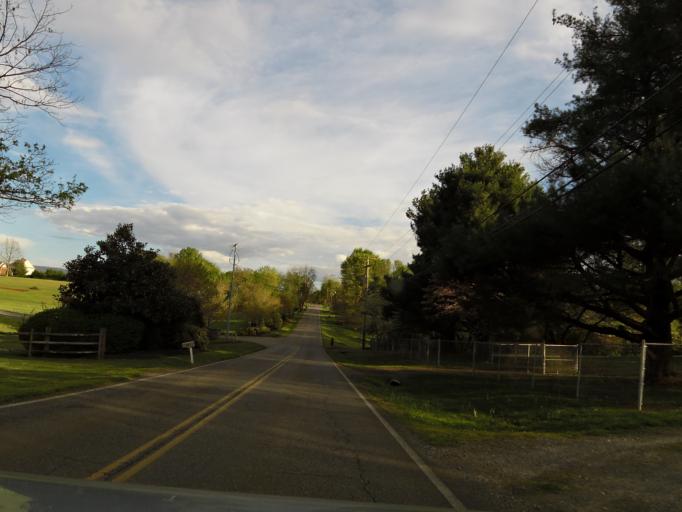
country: US
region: Tennessee
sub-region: Blount County
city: Maryville
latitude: 35.6909
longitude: -84.0194
